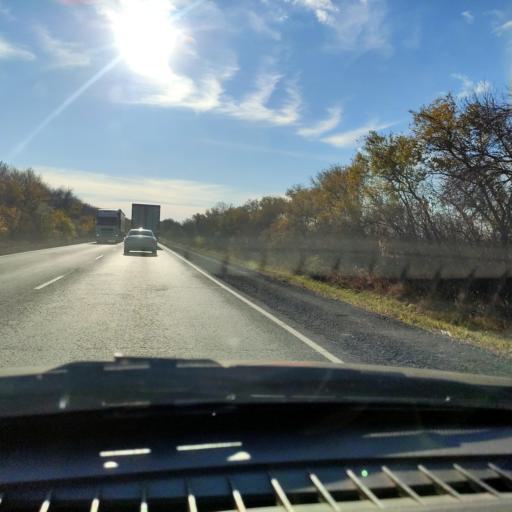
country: RU
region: Samara
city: Zhigulevsk
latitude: 53.2998
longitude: 49.3425
